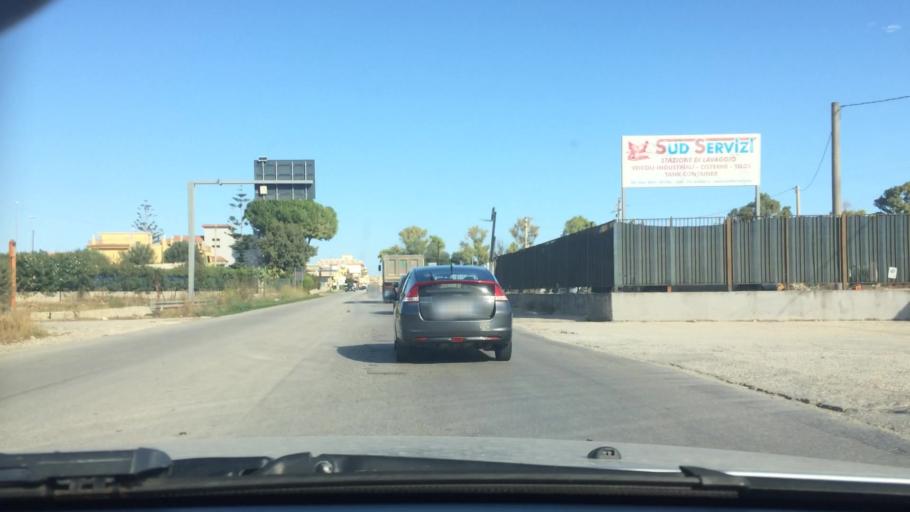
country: IT
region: Sicily
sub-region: Provincia di Siracusa
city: Priolo Gargallo
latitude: 37.1497
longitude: 15.1939
